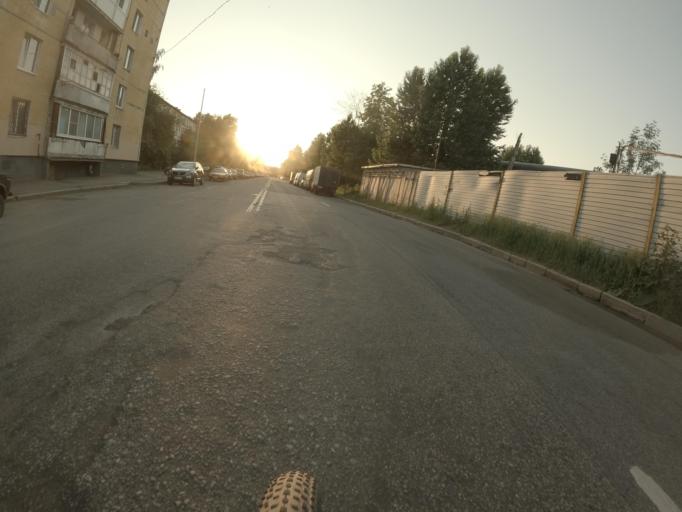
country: RU
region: St.-Petersburg
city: Avtovo
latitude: 59.8675
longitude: 30.2800
